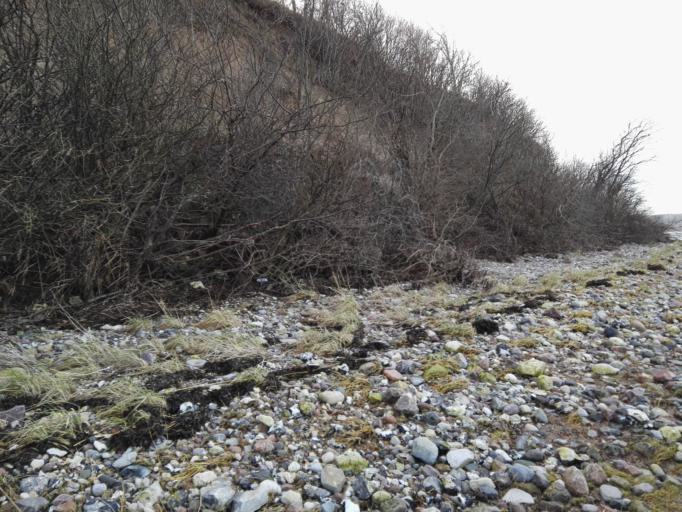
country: DK
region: Capital Region
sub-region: Frederikssund Kommune
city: Frederikssund
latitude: 55.8584
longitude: 12.0477
